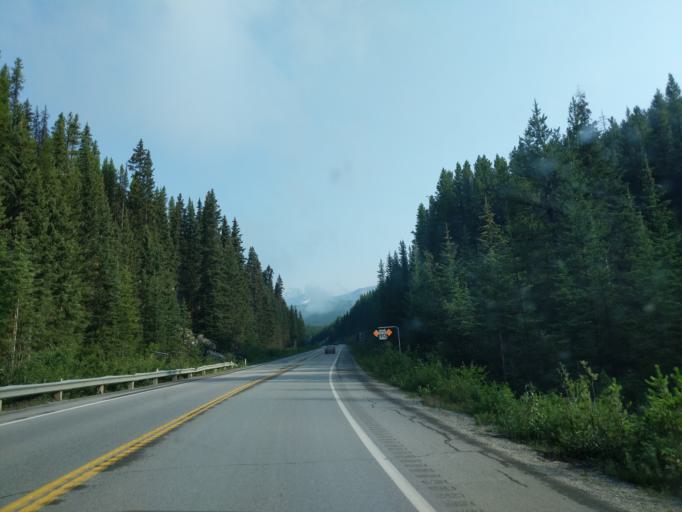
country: CA
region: Alberta
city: Lake Louise
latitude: 51.4463
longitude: -116.2142
